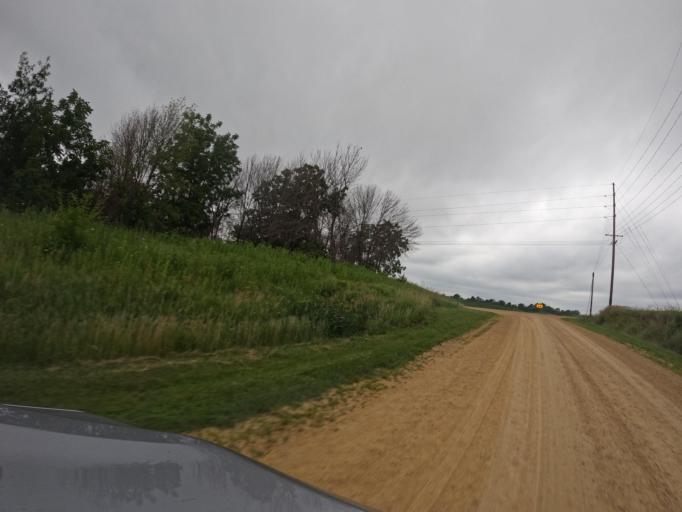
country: US
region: Iowa
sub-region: Jackson County
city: Maquoketa
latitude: 41.9382
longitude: -90.6449
